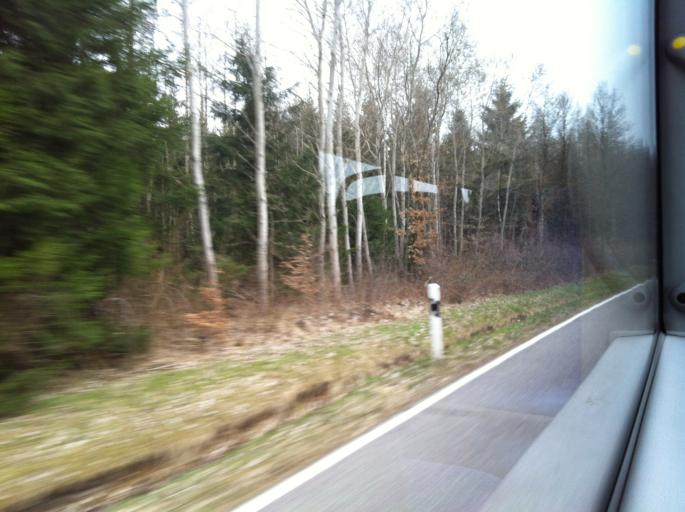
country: DE
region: Baden-Wuerttemberg
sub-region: Karlsruhe Region
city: Limbach
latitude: 49.4931
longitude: 9.2135
